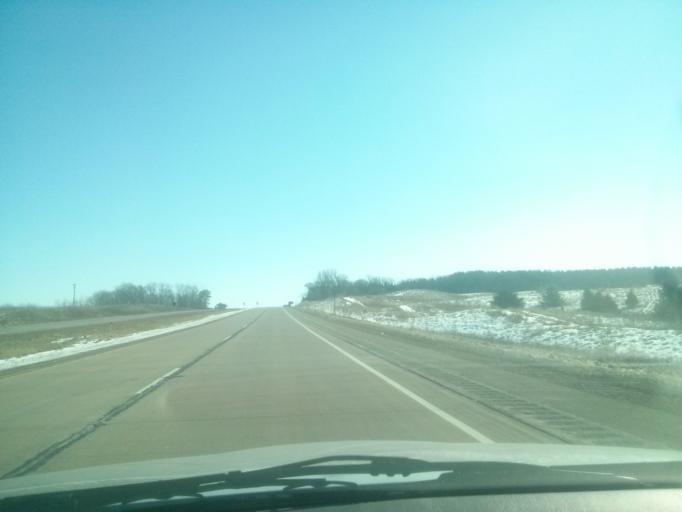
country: US
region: Wisconsin
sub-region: Saint Croix County
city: New Richmond
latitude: 45.1226
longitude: -92.6048
